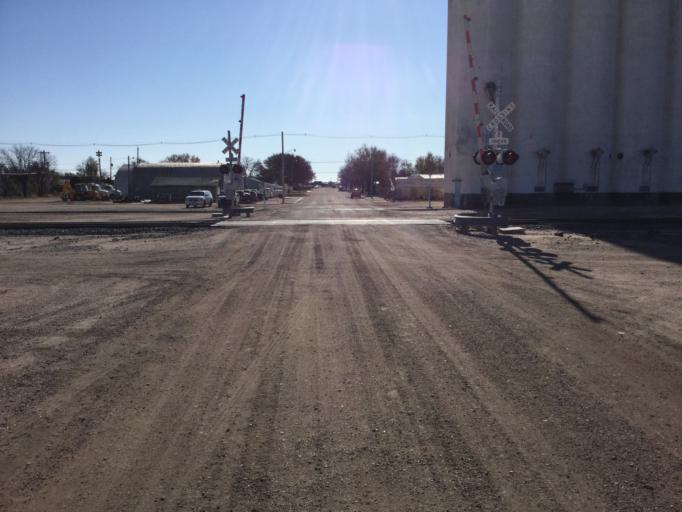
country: US
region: Kansas
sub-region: Kearny County
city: Lakin
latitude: 37.9383
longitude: -101.2561
